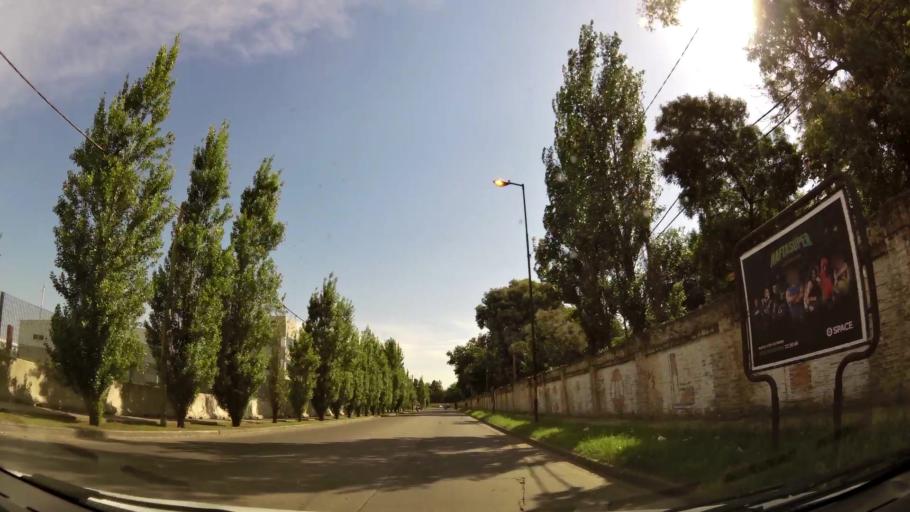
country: AR
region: Buenos Aires
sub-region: Partido de Merlo
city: Merlo
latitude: -34.6352
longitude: -58.7122
